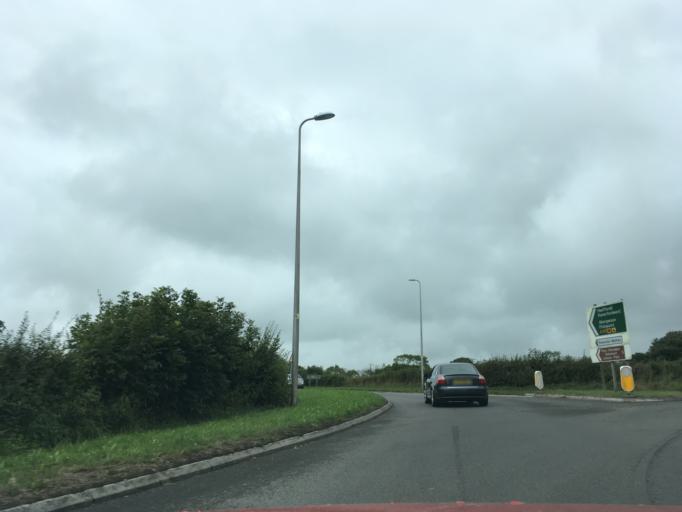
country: GB
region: Wales
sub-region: Pembrokeshire
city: Narberth
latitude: 51.8166
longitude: -4.7287
